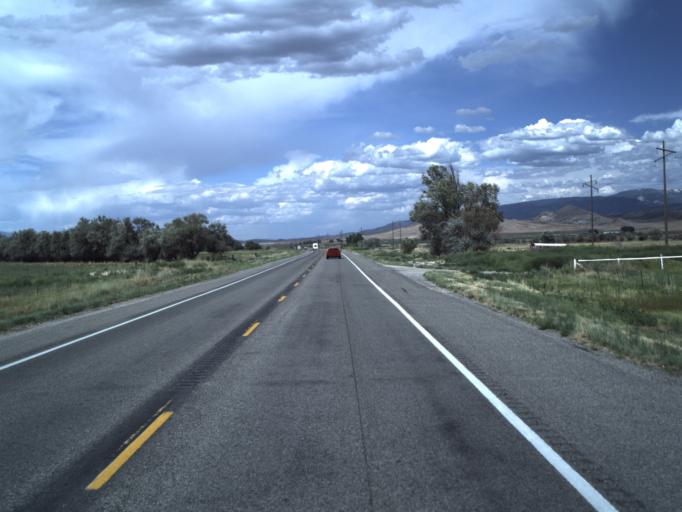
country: US
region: Utah
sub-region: Sevier County
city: Salina
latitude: 38.9769
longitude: -111.8567
